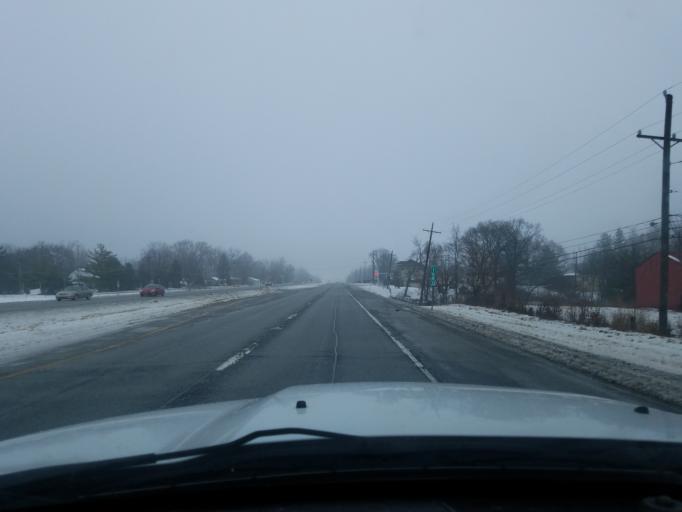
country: US
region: Indiana
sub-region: Cass County
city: Galveston
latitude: 40.5552
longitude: -86.1270
